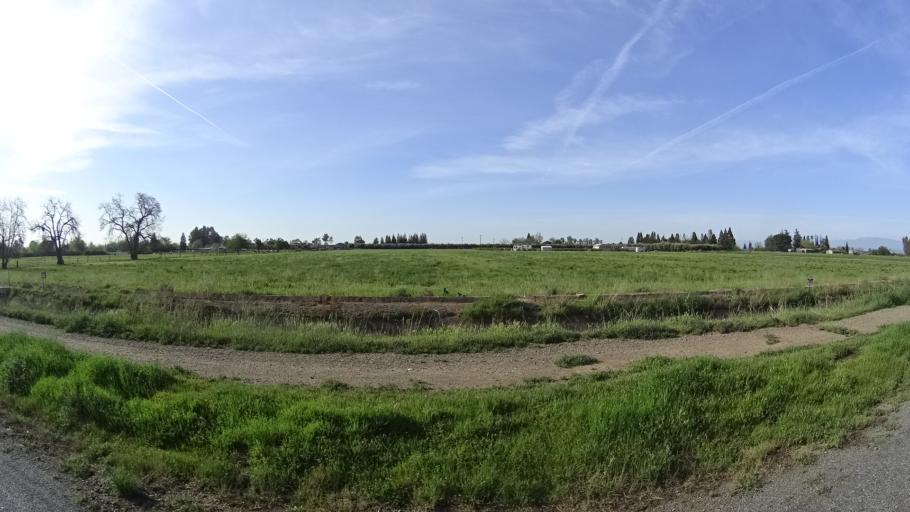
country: US
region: California
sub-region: Glenn County
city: Orland
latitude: 39.7189
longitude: -122.2210
